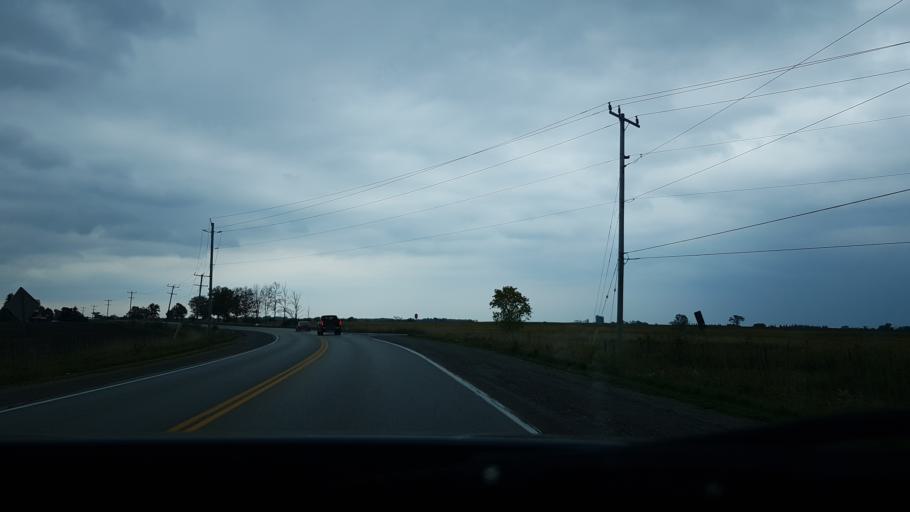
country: CA
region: Ontario
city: Omemee
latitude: 44.3623
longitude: -78.7087
